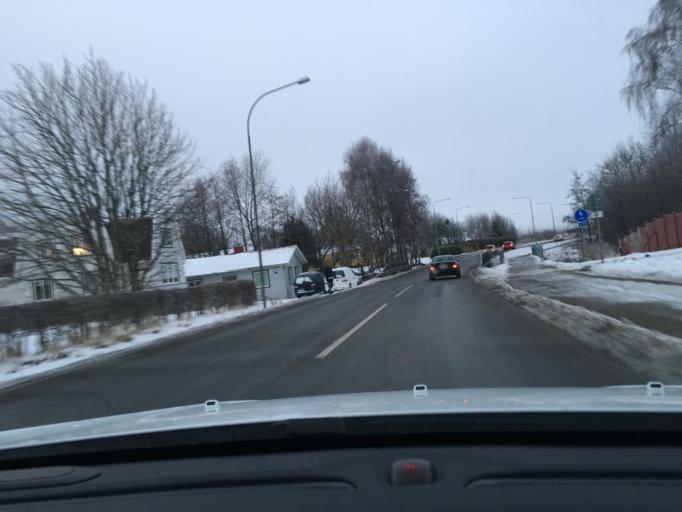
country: SE
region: Vaestra Goetaland
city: Svanesund
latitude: 58.1020
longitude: 11.8496
